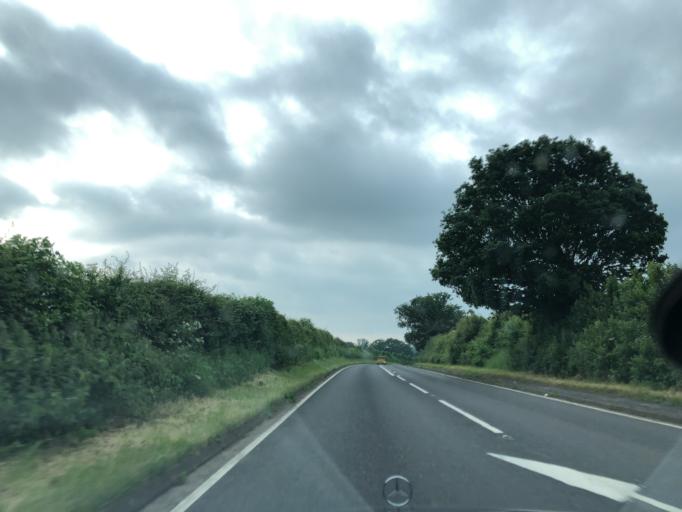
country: GB
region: England
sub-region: Warwickshire
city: Wroxall
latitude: 52.3116
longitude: -1.6649
